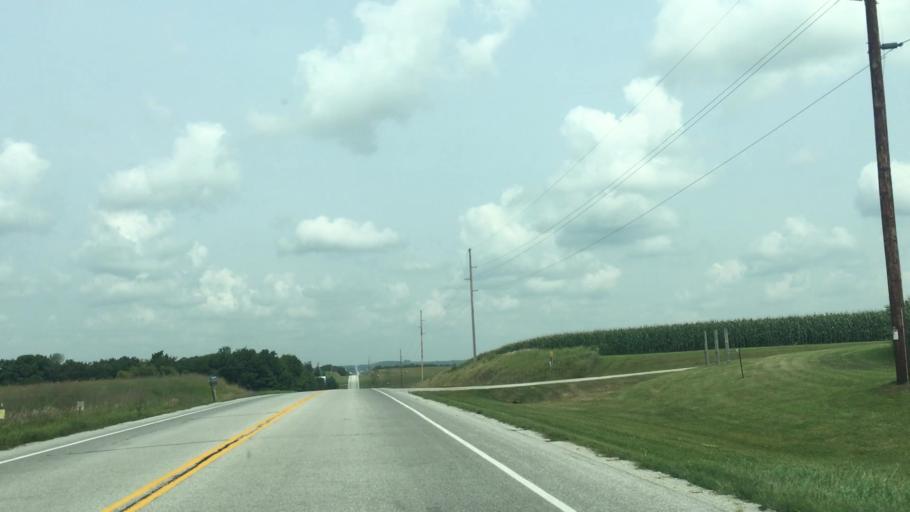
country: US
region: Minnesota
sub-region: Fillmore County
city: Harmony
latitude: 43.5701
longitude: -91.9298
